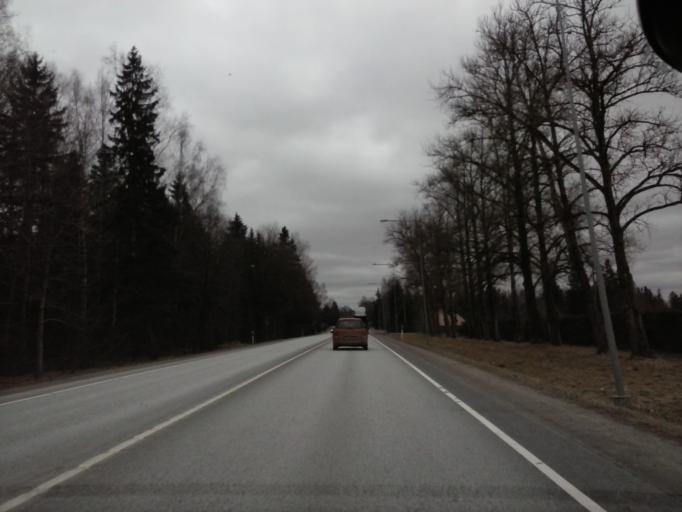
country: EE
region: Jaervamaa
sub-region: Paide linn
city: Paide
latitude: 59.0076
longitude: 25.5955
